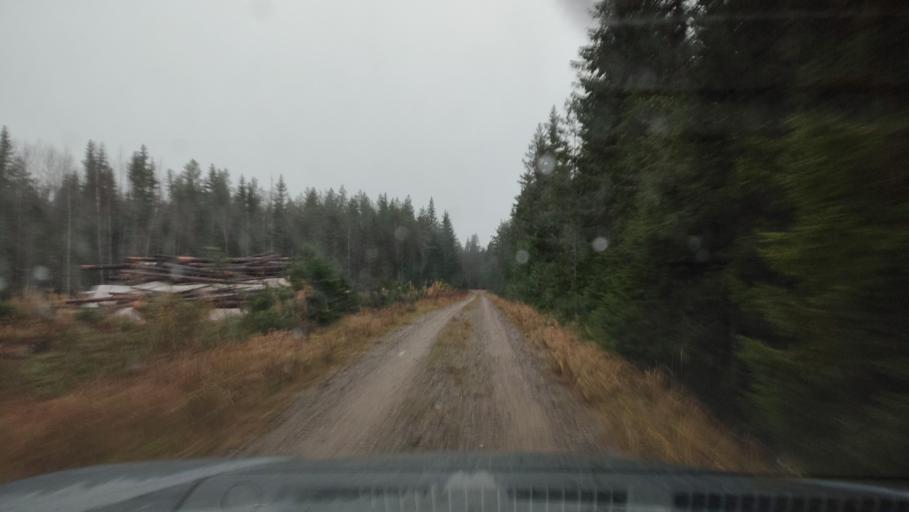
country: FI
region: Southern Ostrobothnia
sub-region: Suupohja
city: Karijoki
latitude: 62.1814
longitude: 21.7315
